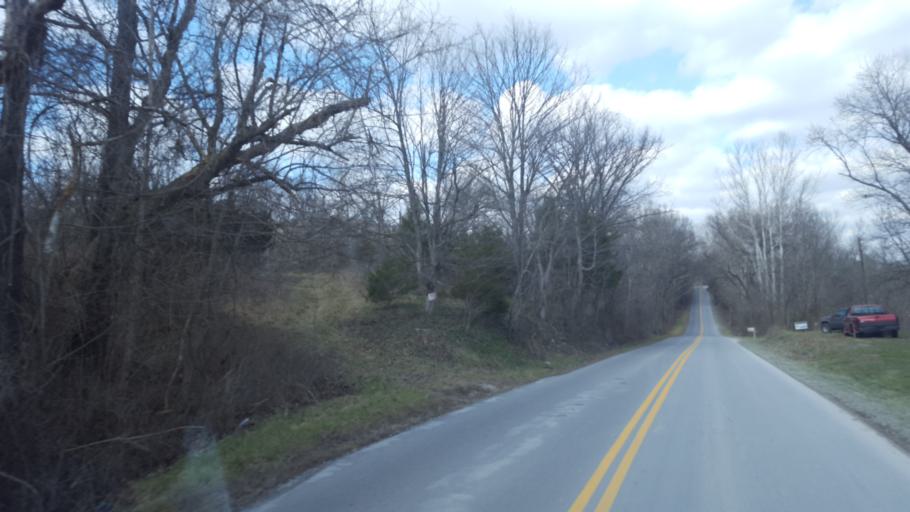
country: US
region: Kentucky
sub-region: Owen County
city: Owenton
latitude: 38.4559
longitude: -84.9585
